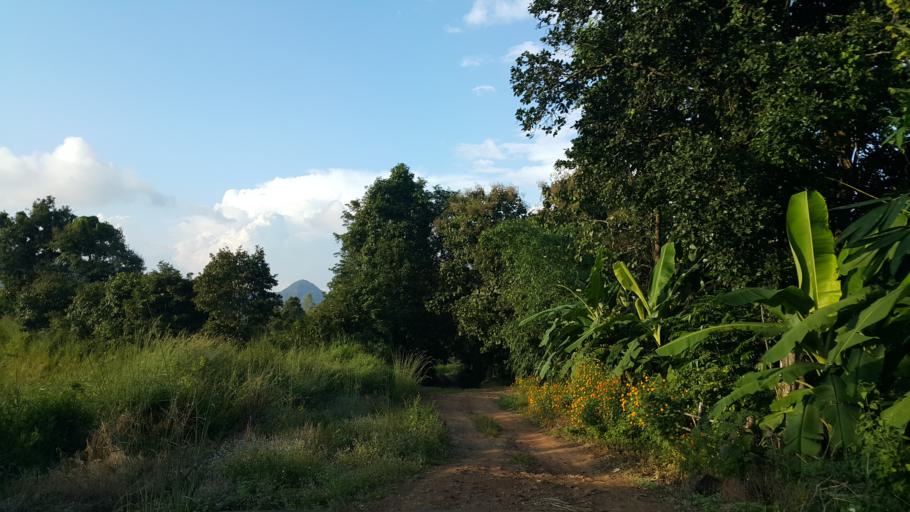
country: TH
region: Chiang Mai
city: Mae On
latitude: 18.7406
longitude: 99.2506
